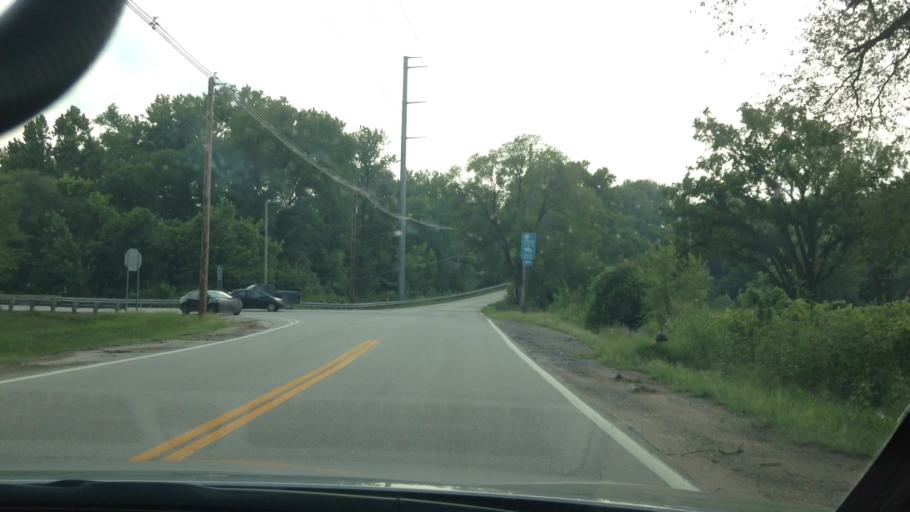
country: US
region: Kansas
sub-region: Leavenworth County
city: Lansing
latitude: 39.1871
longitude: -94.8023
